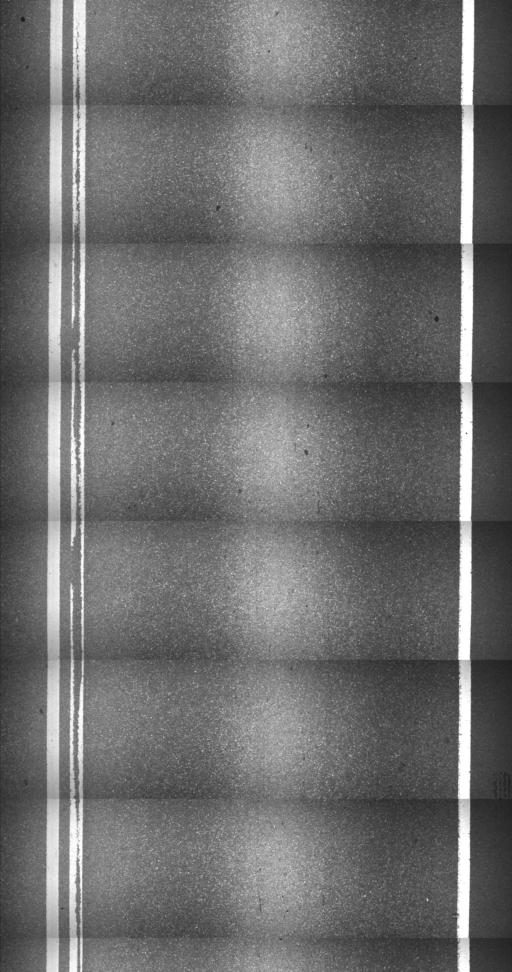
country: US
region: Vermont
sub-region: Washington County
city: Waterbury
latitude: 44.2038
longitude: -72.8094
